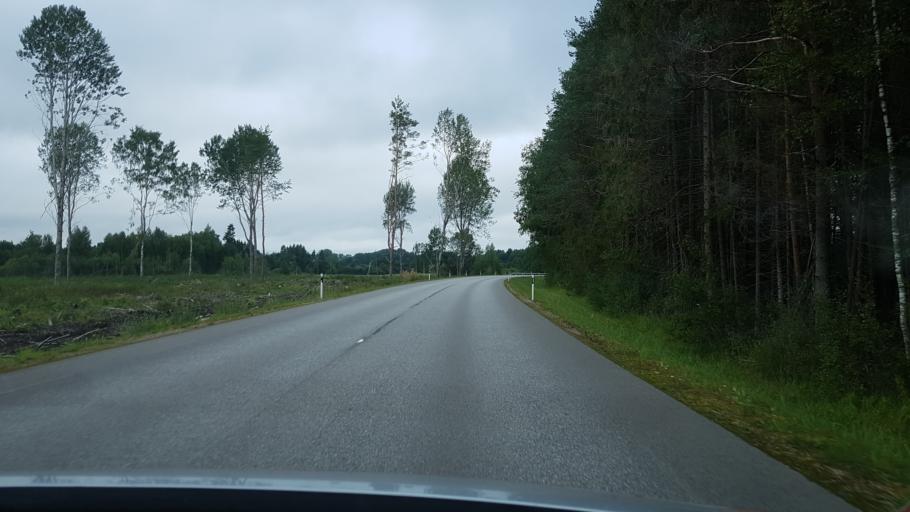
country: EE
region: Valgamaa
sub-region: Valga linn
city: Valga
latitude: 57.7333
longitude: 26.1502
